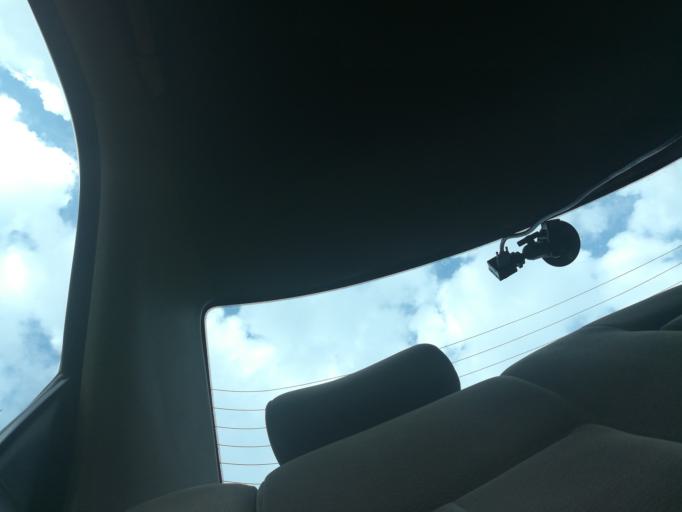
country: NG
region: Lagos
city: Ikorodu
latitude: 6.6610
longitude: 3.5902
